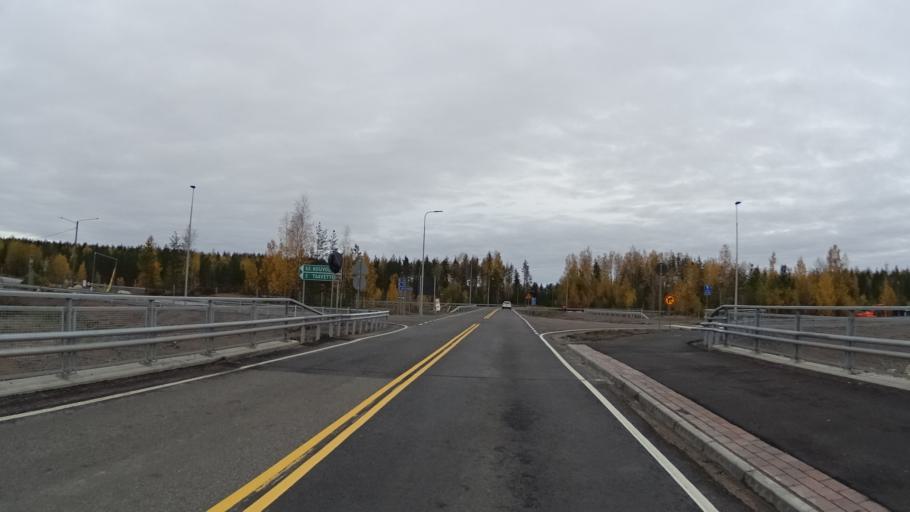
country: FI
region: South Karelia
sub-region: Lappeenranta
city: Luumaeki
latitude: 60.9289
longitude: 27.6309
